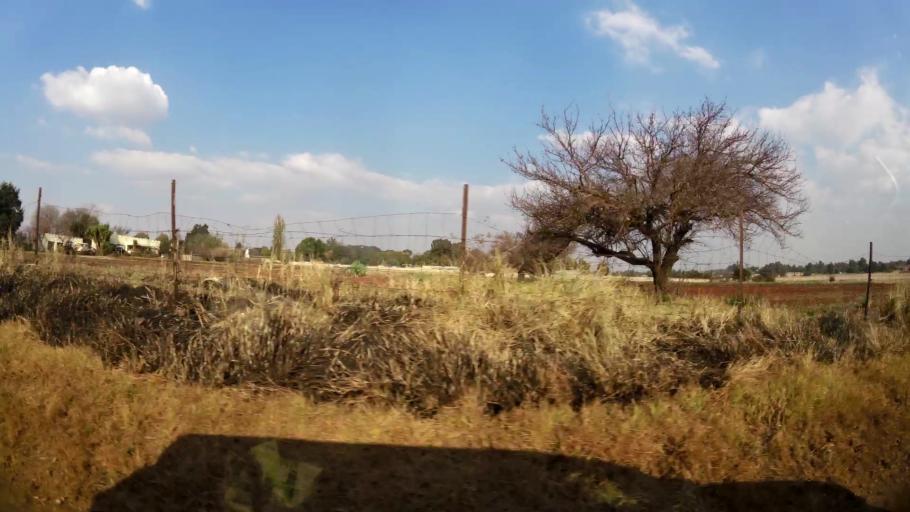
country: ZA
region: Gauteng
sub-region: Ekurhuleni Metropolitan Municipality
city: Benoni
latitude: -26.0947
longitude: 28.2866
